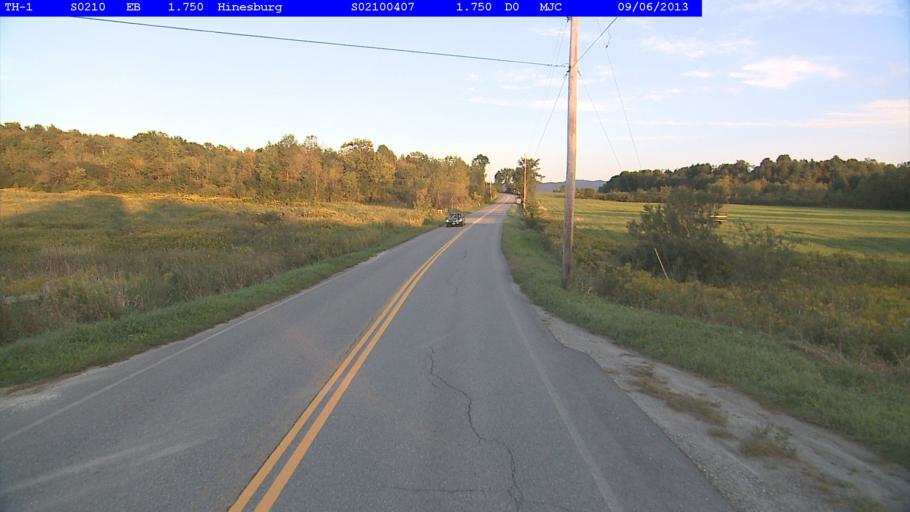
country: US
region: Vermont
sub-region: Chittenden County
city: Hinesburg
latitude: 44.3439
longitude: -73.1390
